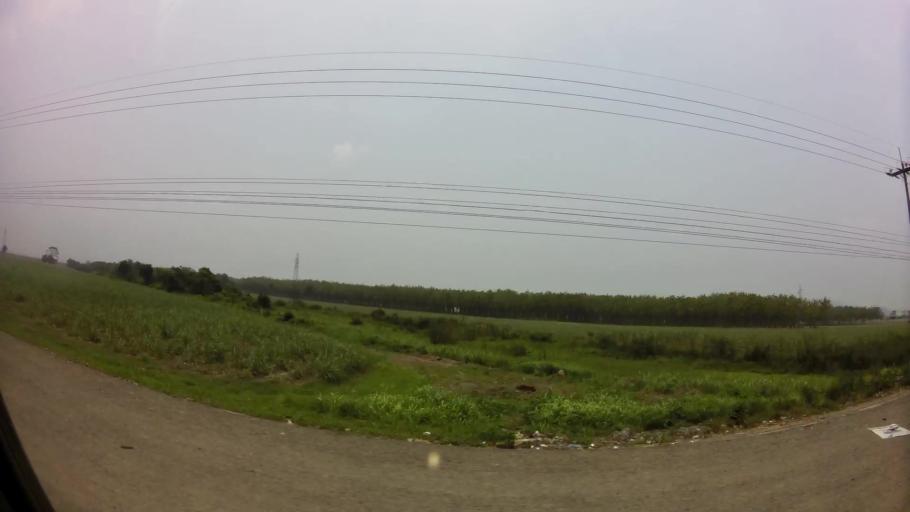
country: HN
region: Cortes
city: La Lima
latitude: 15.4116
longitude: -87.8734
